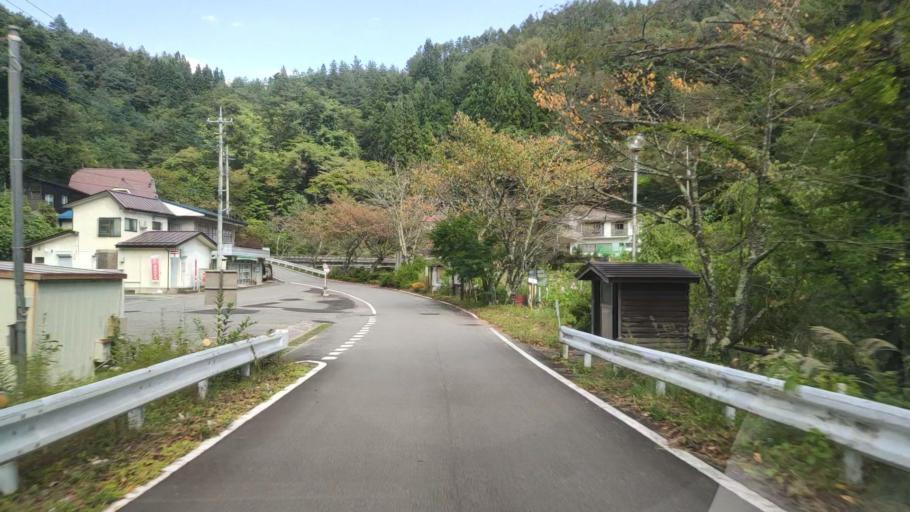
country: JP
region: Gunma
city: Nakanojomachi
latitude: 36.6469
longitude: 138.6488
